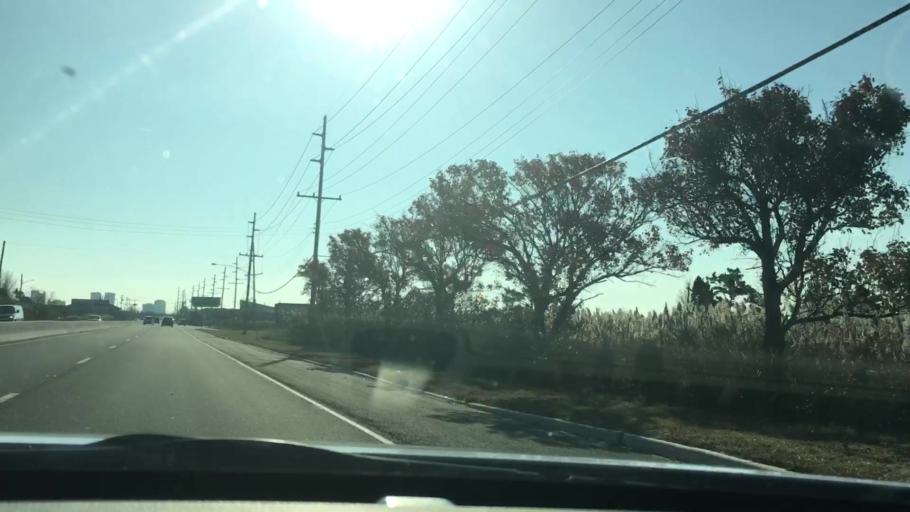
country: US
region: New Jersey
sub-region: Atlantic County
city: Ventnor City
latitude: 39.3742
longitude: -74.4819
